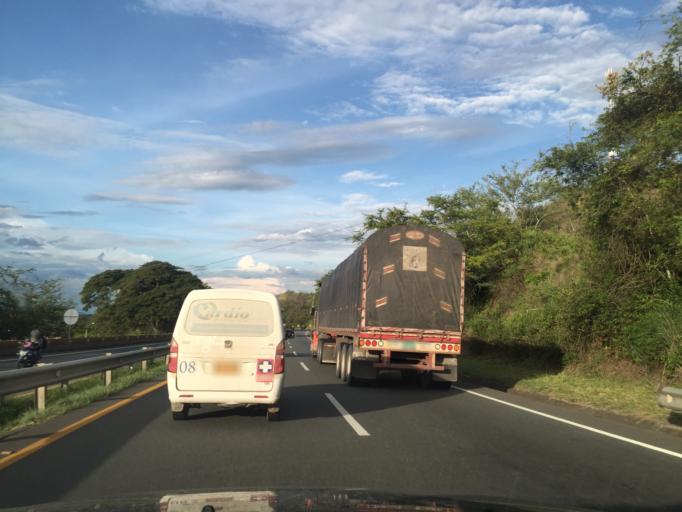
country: CO
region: Valle del Cauca
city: Bugalagrande
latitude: 4.2106
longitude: -76.1519
